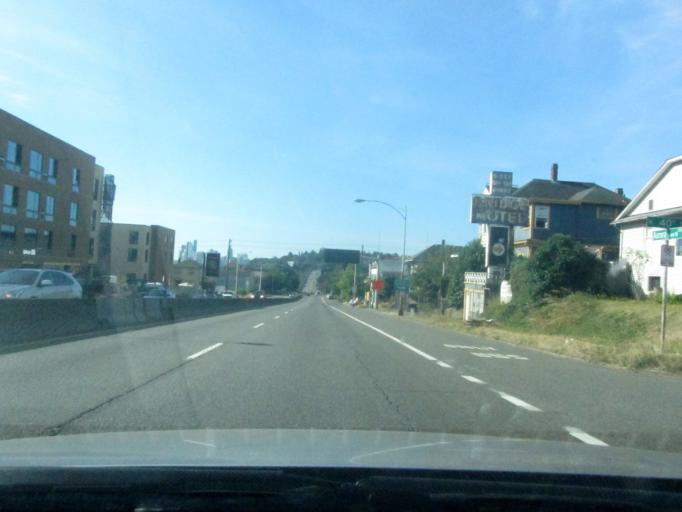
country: US
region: Washington
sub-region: King County
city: Seattle
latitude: 47.6554
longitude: -122.3475
